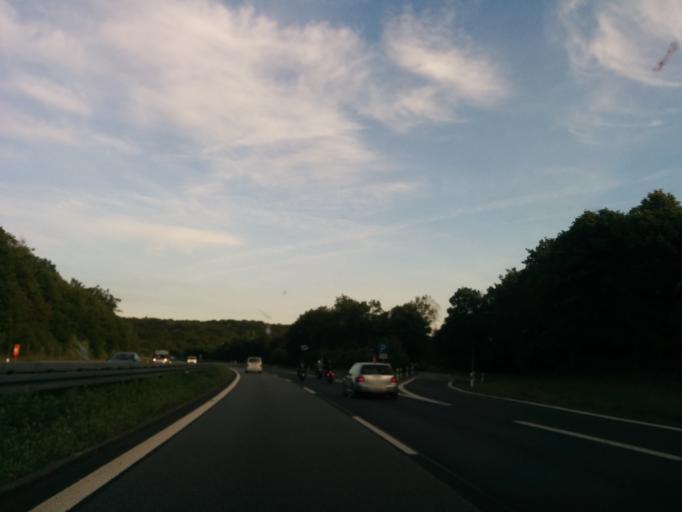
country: DE
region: Bavaria
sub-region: Regierungsbezirk Unterfranken
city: Wasserlosen
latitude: 50.0841
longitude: 9.9879
